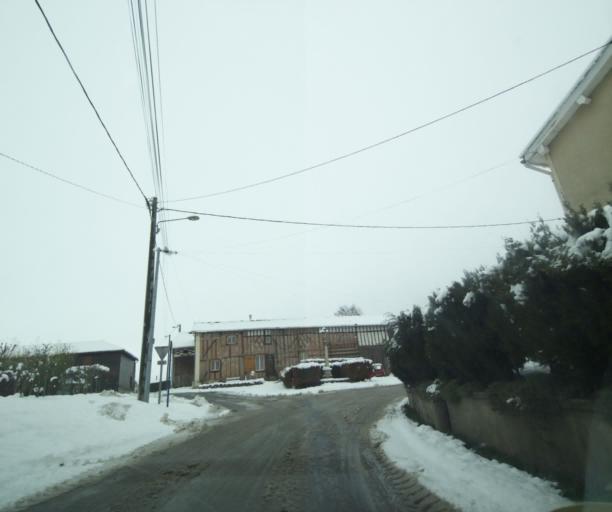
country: FR
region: Champagne-Ardenne
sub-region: Departement de la Haute-Marne
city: Montier-en-Der
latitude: 48.5064
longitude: 4.7846
